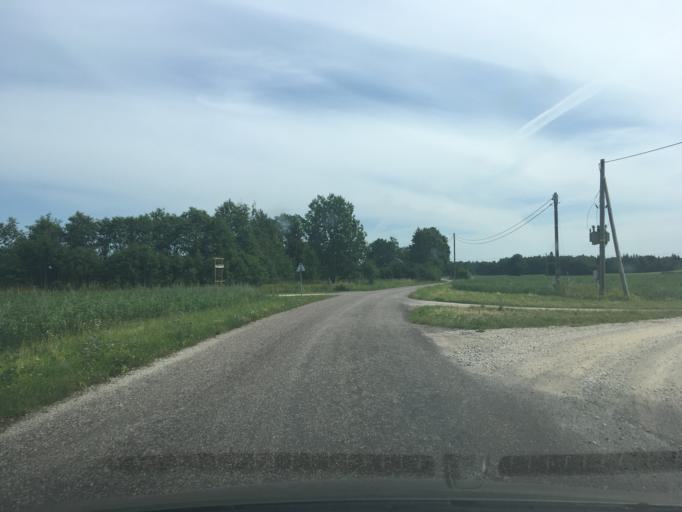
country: EE
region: Raplamaa
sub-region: Rapla vald
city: Rapla
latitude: 59.0297
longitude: 24.8039
